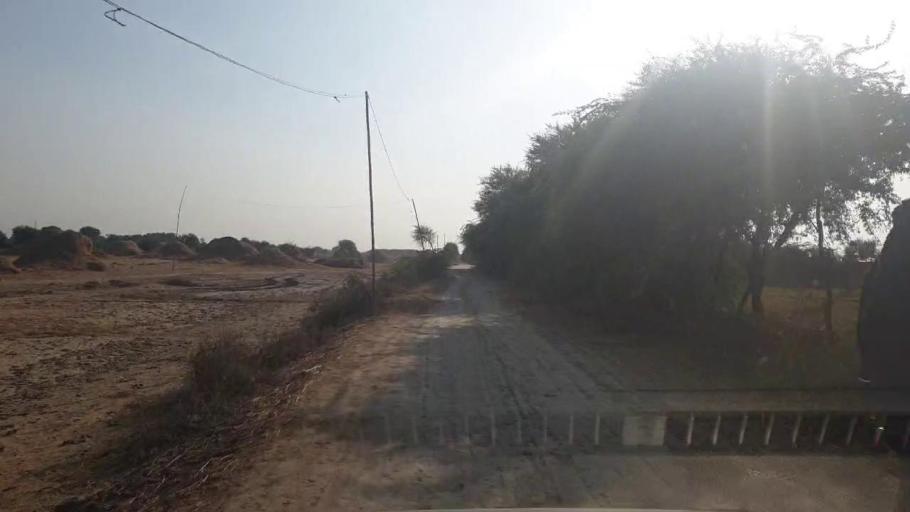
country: PK
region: Sindh
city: Badin
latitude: 24.6428
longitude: 68.8026
